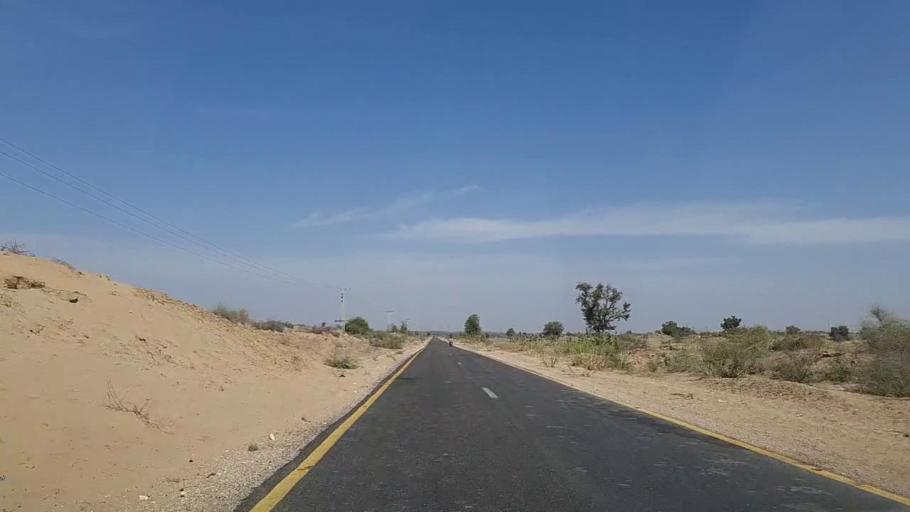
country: PK
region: Sindh
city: Mithi
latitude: 24.9542
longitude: 69.9044
